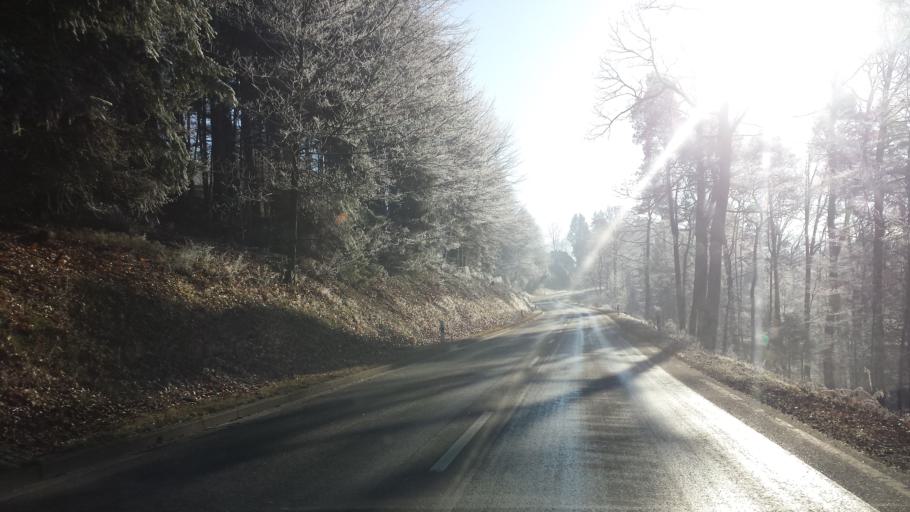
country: DE
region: Baden-Wuerttemberg
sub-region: Karlsruhe Region
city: Wilhelmsfeld
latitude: 49.4762
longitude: 8.7480
